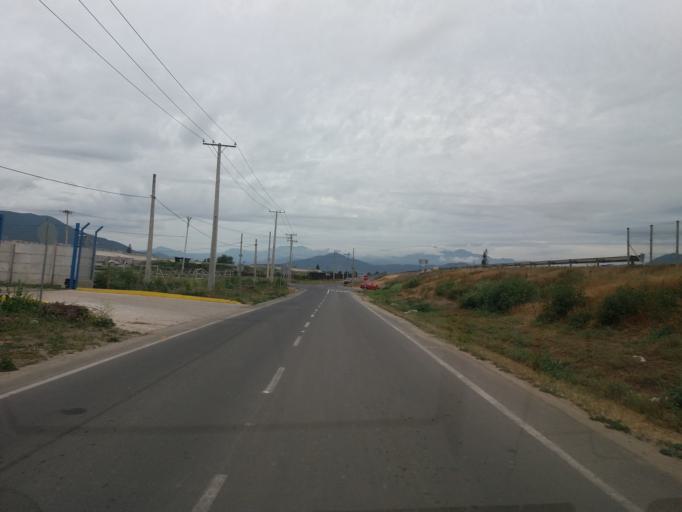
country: CL
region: Valparaiso
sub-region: Provincia de Quillota
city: Quillota
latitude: -32.9185
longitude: -71.2766
